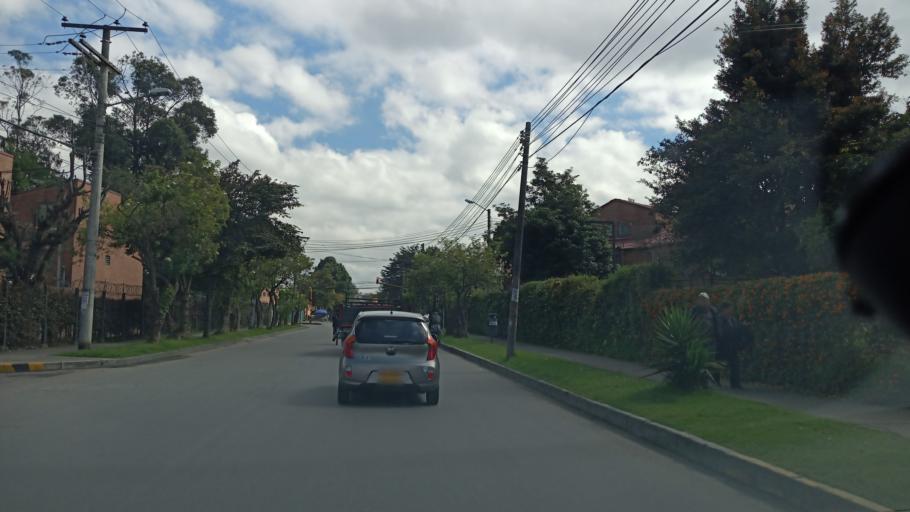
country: CO
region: Bogota D.C.
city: Bogota
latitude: 4.6809
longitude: -74.1316
